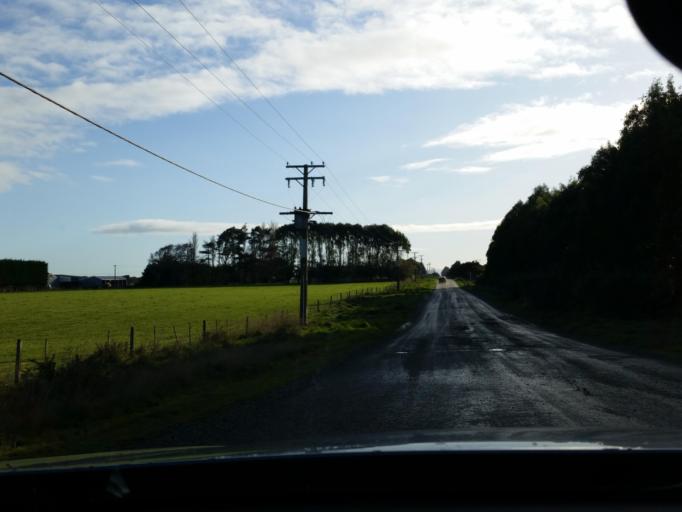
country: NZ
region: Southland
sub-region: Invercargill City
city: Invercargill
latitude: -46.3385
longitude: 168.4535
